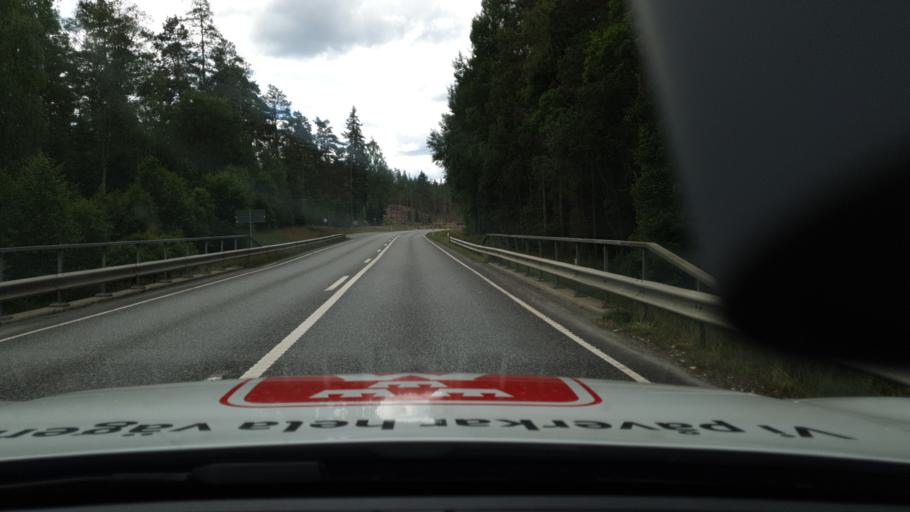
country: SE
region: Joenkoeping
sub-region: Mullsjo Kommun
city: Mullsjoe
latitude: 57.7463
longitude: 13.8889
